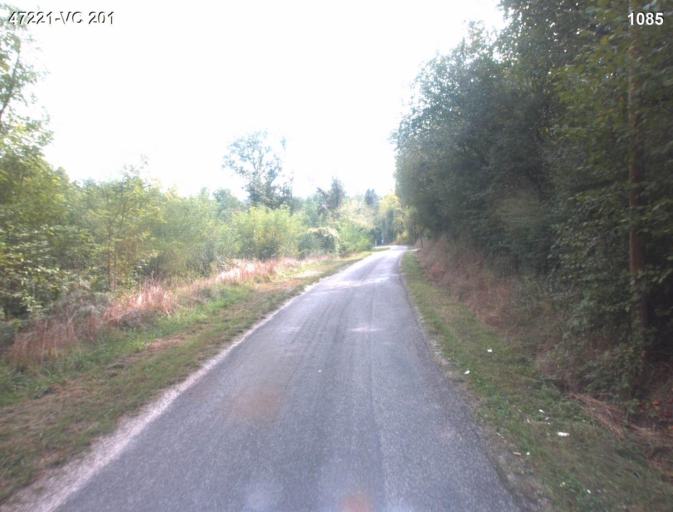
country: FR
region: Aquitaine
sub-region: Departement du Lot-et-Garonne
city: Mezin
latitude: 44.1135
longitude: 0.2331
